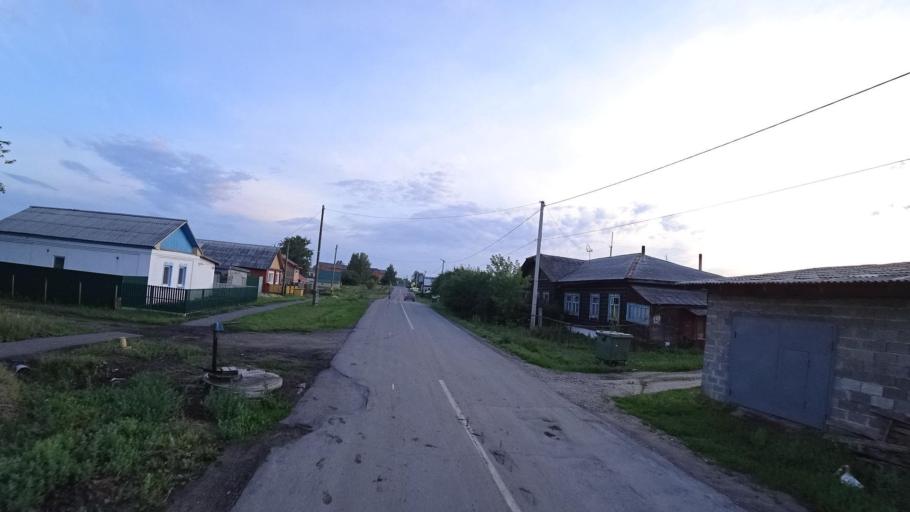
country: RU
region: Sverdlovsk
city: Kamyshlov
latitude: 56.8560
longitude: 62.6991
